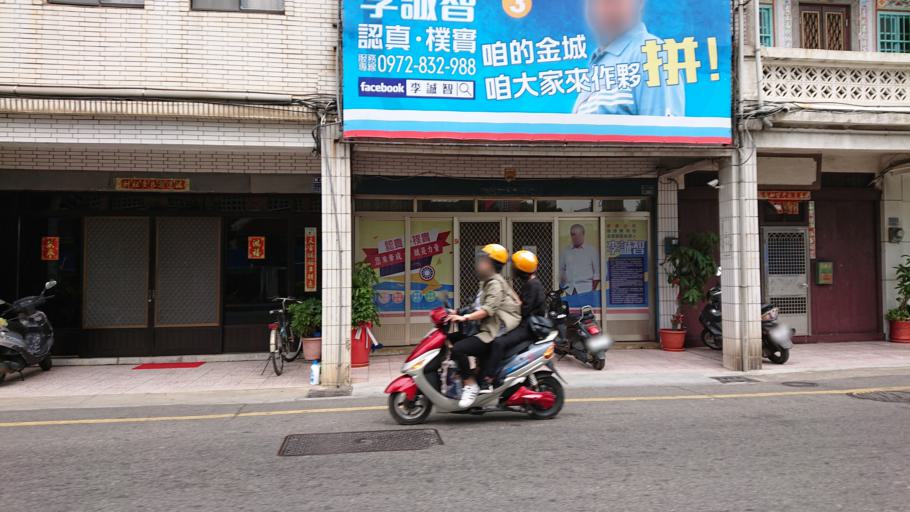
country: TW
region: Fukien
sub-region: Kinmen
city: Jincheng
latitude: 24.4304
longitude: 118.3148
